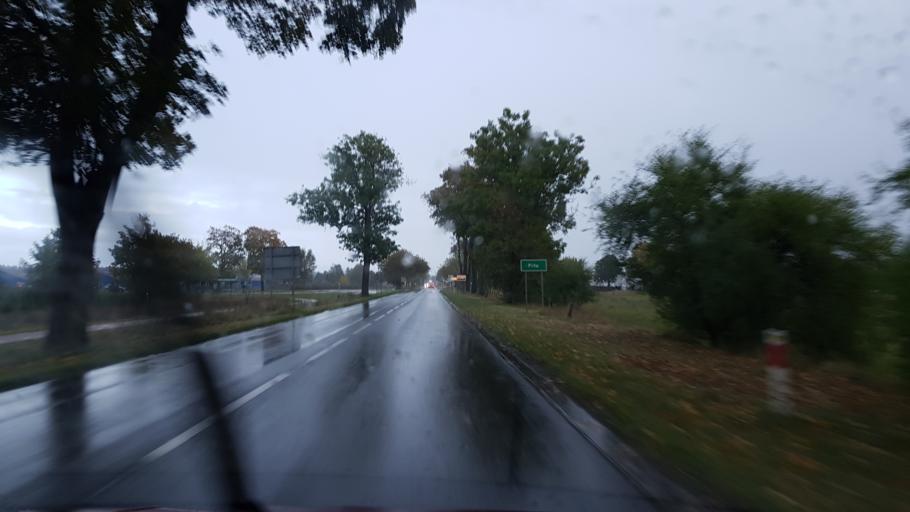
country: PL
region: Greater Poland Voivodeship
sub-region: Powiat pilski
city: Pila
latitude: 53.1555
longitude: 16.6816
